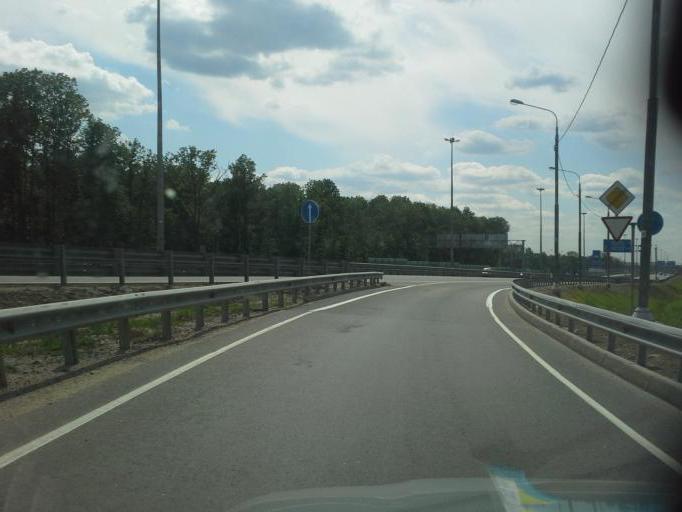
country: RU
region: Moskovskaya
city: Odintsovo
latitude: 55.6928
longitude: 37.2672
